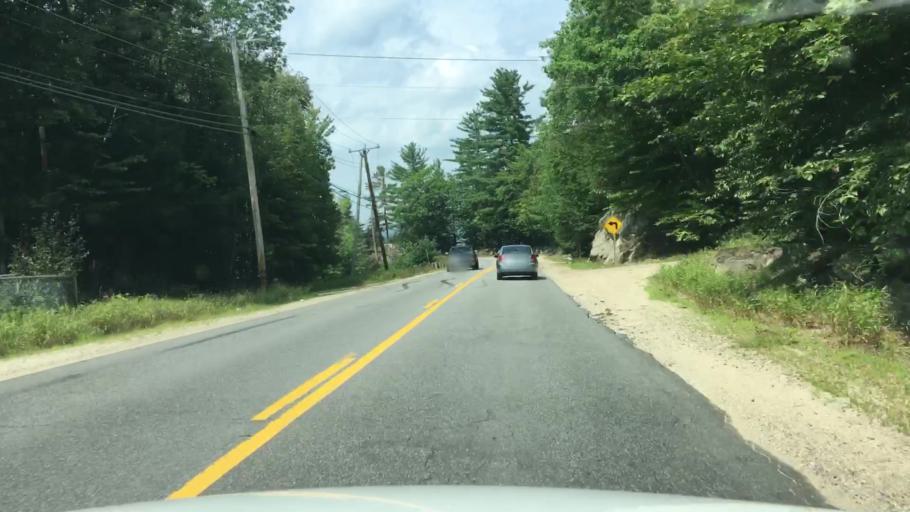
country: US
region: Maine
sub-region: Oxford County
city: Rumford
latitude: 44.5353
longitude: -70.5412
